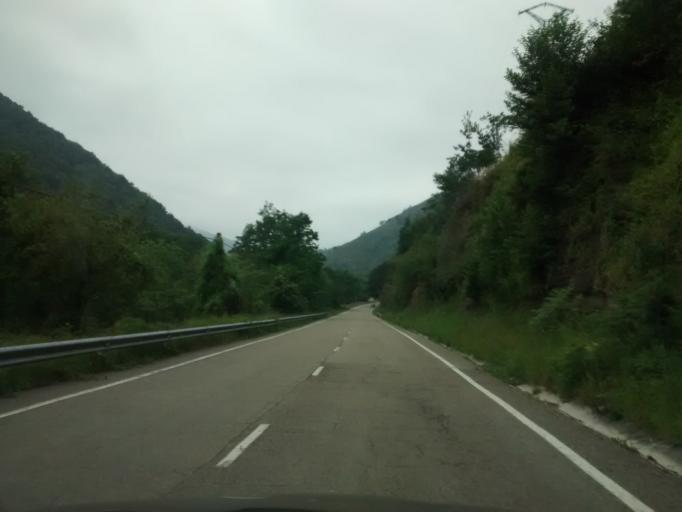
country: ES
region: Cantabria
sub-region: Provincia de Cantabria
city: Ruente
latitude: 43.1618
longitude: -4.2533
